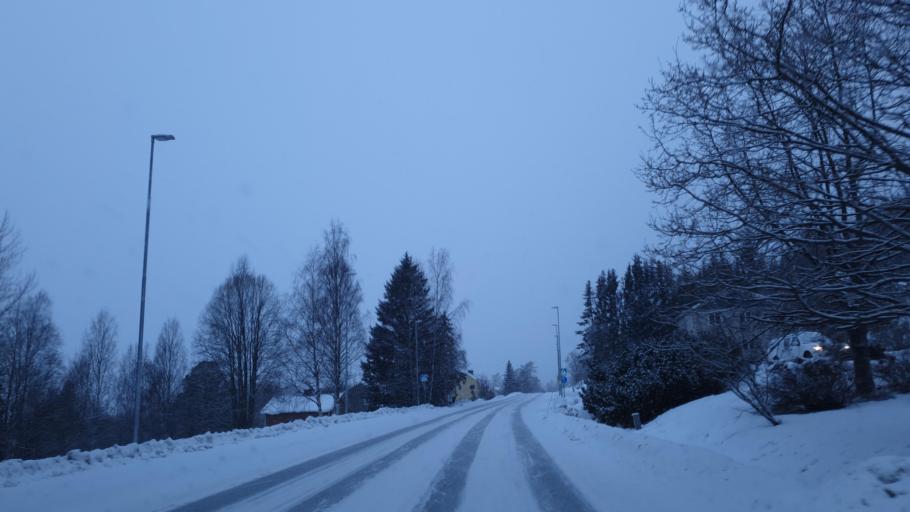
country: SE
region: Vaesternorrland
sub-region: OErnskoeldsviks Kommun
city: Ornskoldsvik
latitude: 63.2981
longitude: 18.6666
